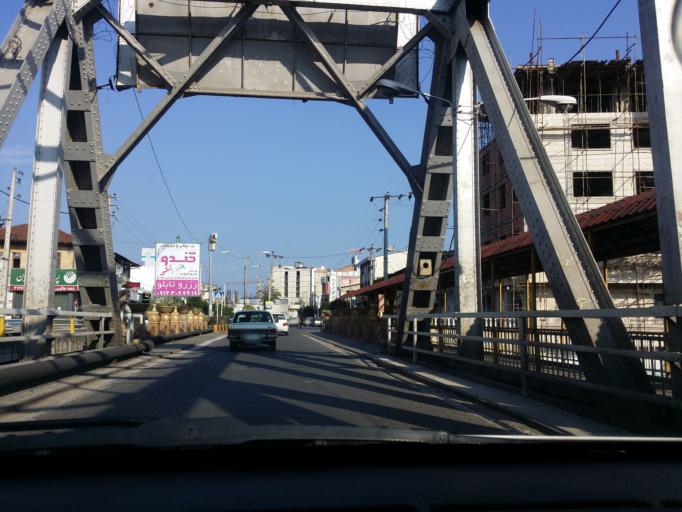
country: IR
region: Mazandaran
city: Chalus
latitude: 36.6524
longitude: 51.4219
